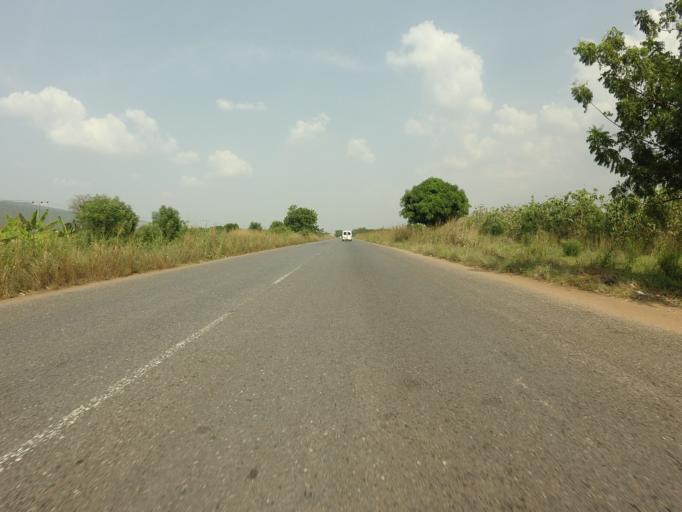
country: GH
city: Akropong
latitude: 5.9306
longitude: -0.0393
